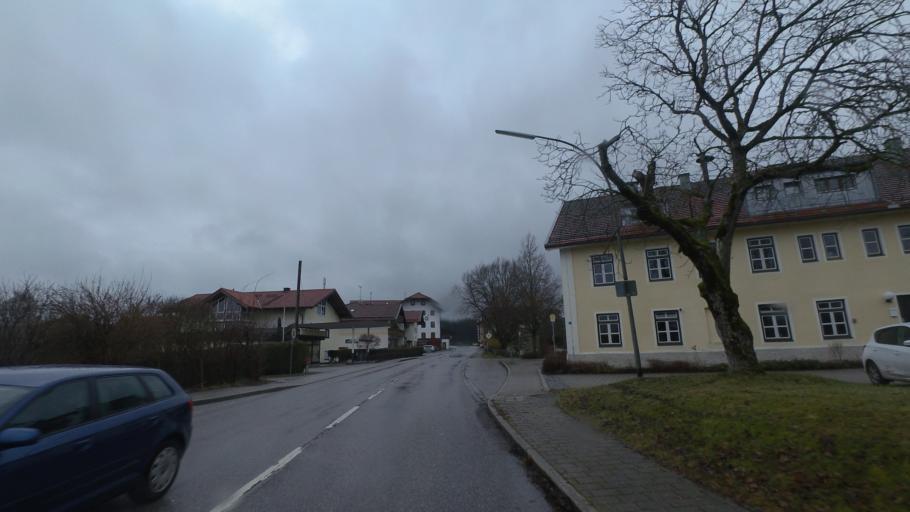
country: DE
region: Bavaria
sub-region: Upper Bavaria
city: Sankt Leonhard am Wonneberg
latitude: 47.9380
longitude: 12.6990
